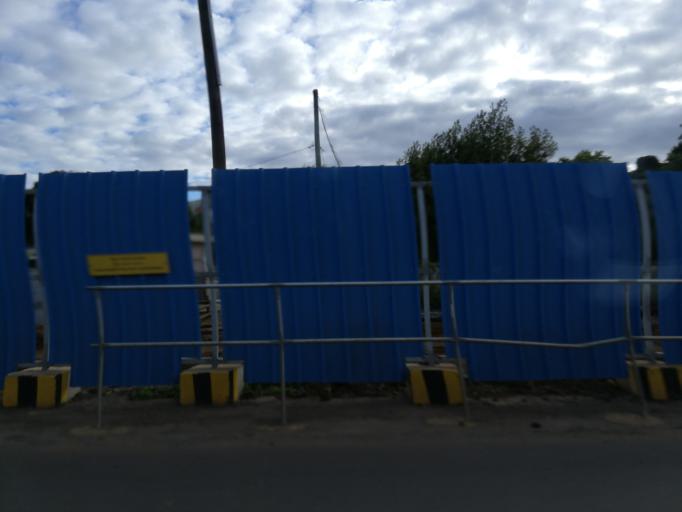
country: MU
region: Plaines Wilhems
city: Ebene
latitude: -20.2287
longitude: 57.4693
